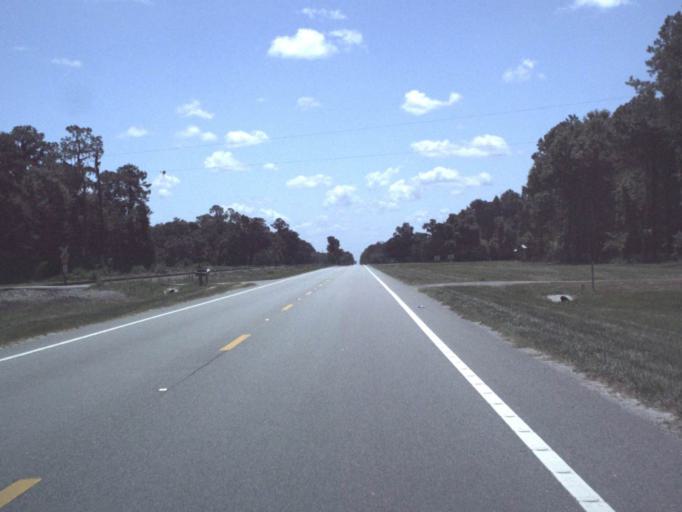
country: US
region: Florida
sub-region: Hamilton County
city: Jasper
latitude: 30.4766
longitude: -82.9131
